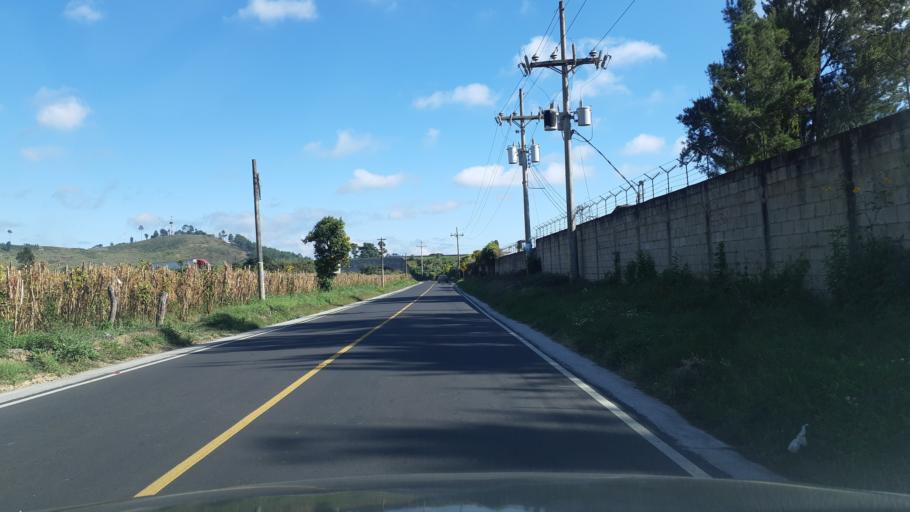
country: GT
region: Chimaltenango
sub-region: Municipio de Chimaltenango
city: Chimaltenango
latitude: 14.6373
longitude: -90.8256
